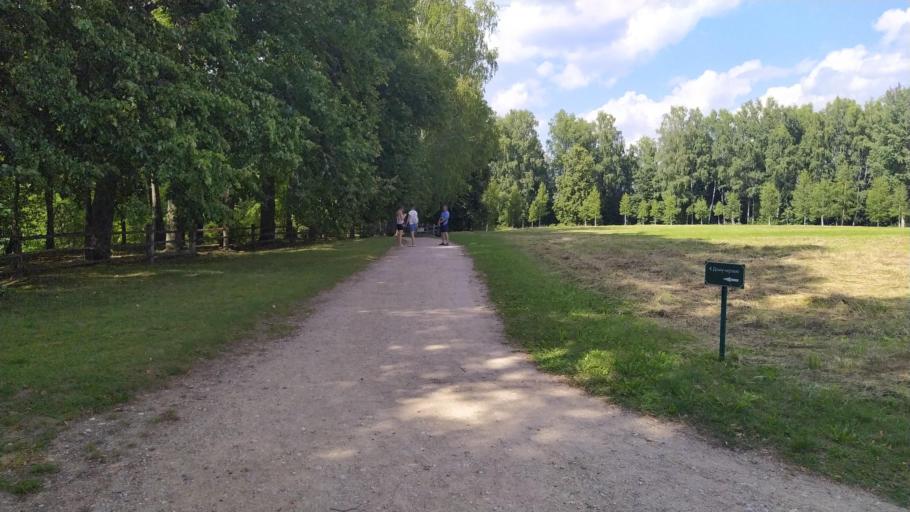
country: RU
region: Pskov
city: Pushkinskiye Gory
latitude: 57.0601
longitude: 28.9239
